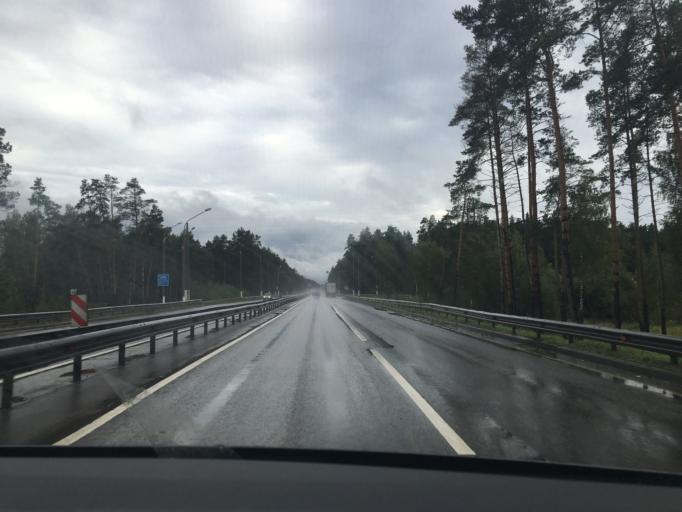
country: RU
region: Kaluga
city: Obninsk
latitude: 55.0674
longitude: 36.6238
